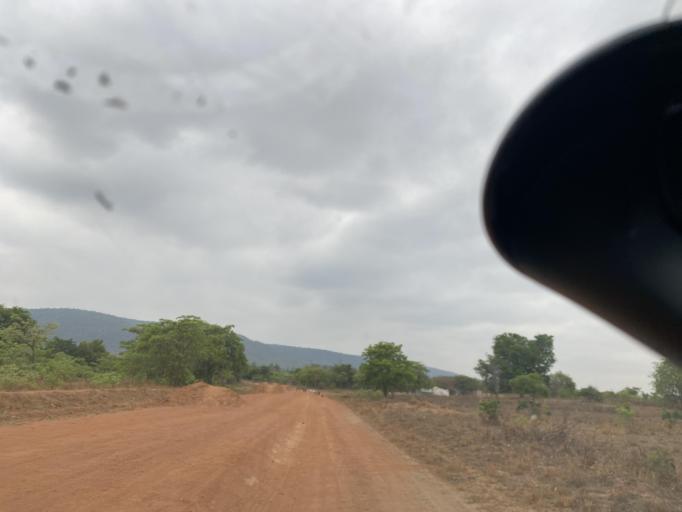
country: ZM
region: Lusaka
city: Chongwe
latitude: -15.1998
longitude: 28.7638
